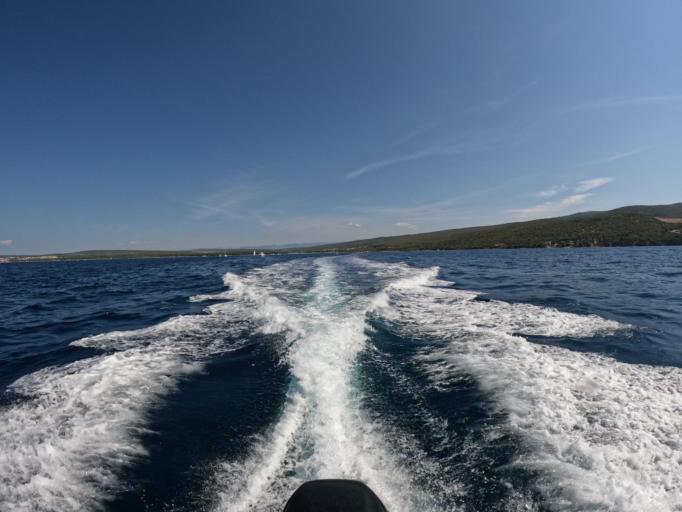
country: HR
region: Primorsko-Goranska
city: Punat
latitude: 44.9906
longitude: 14.6144
